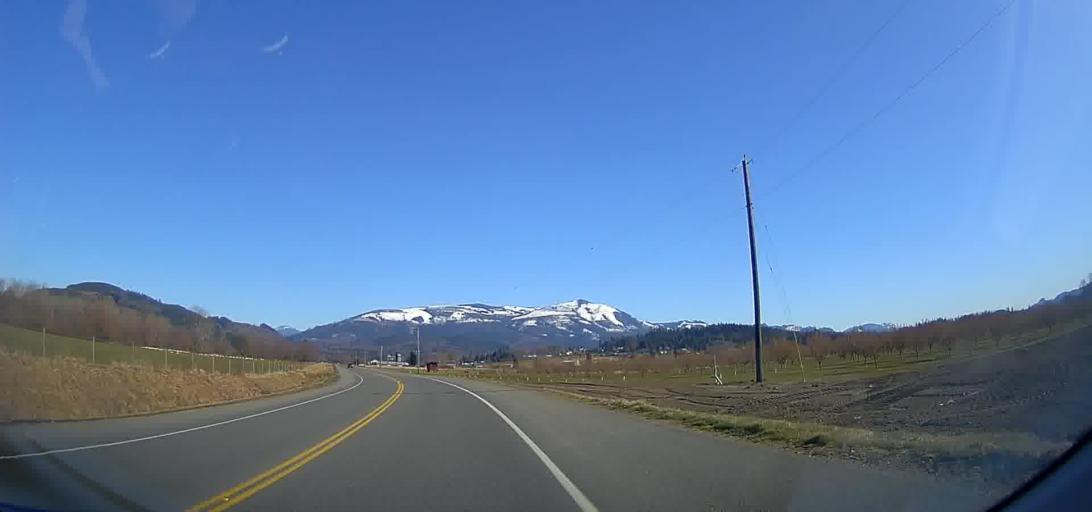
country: US
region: Washington
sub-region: Skagit County
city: Clear Lake
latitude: 48.4644
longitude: -122.2706
